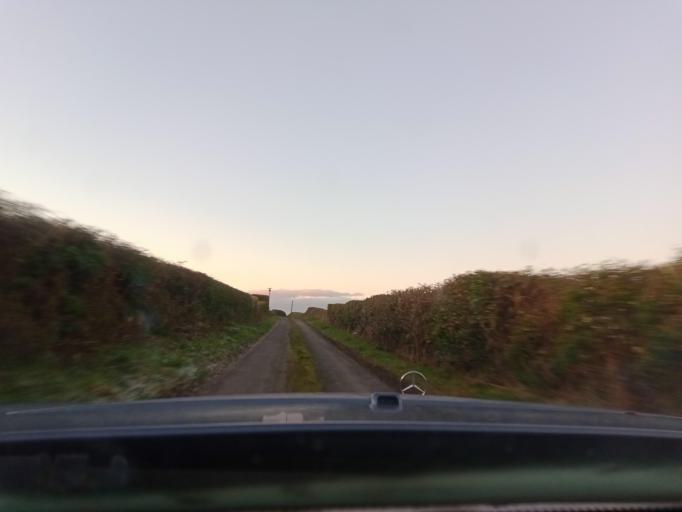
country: IE
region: Leinster
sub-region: Kilkenny
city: Graiguenamanagh
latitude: 52.5790
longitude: -6.9599
